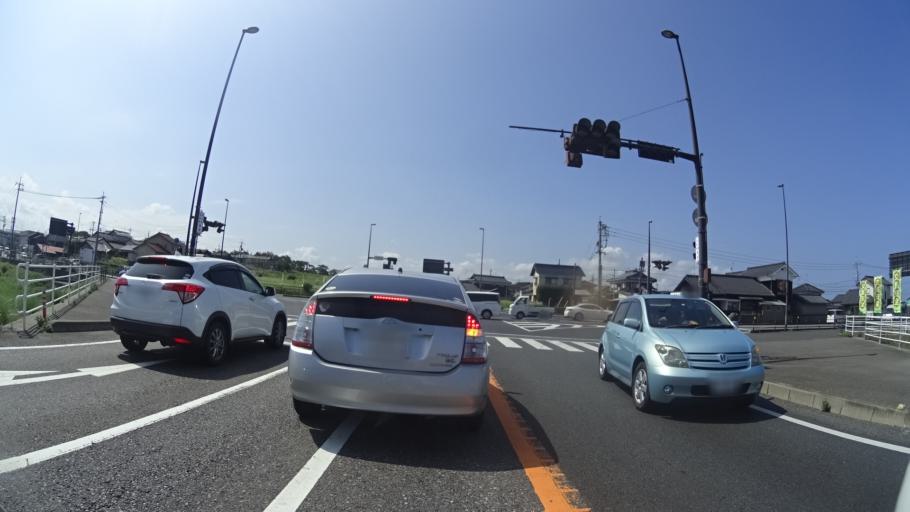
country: JP
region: Shimane
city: Masuda
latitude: 34.6883
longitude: 131.8247
